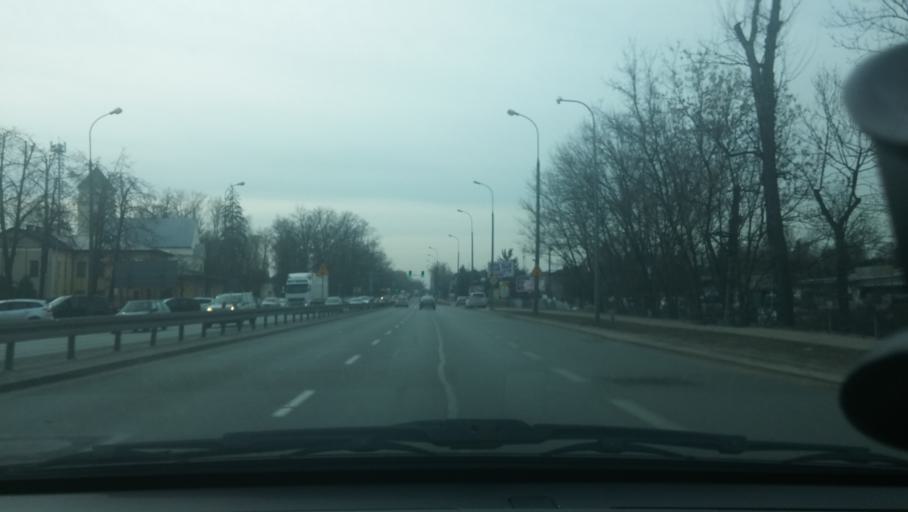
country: PL
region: Masovian Voivodeship
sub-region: Powiat wolominski
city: Slupno
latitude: 52.3629
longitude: 21.1377
